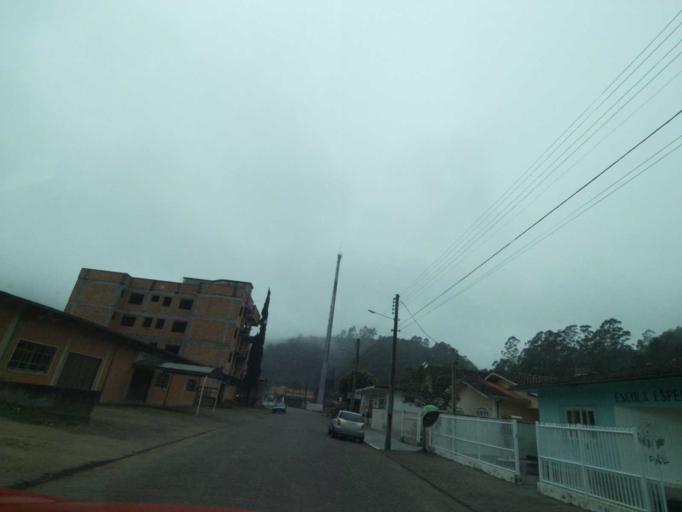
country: BR
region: Santa Catarina
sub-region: Anitapolis
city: Anitapolis
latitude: -27.9057
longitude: -49.1298
